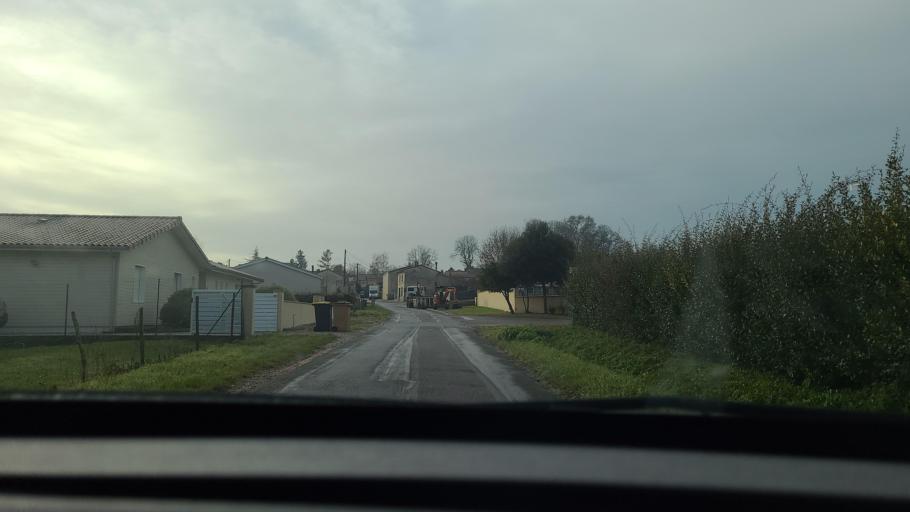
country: FR
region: Aquitaine
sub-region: Departement de la Gironde
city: Marcamps
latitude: 45.0377
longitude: -0.4696
